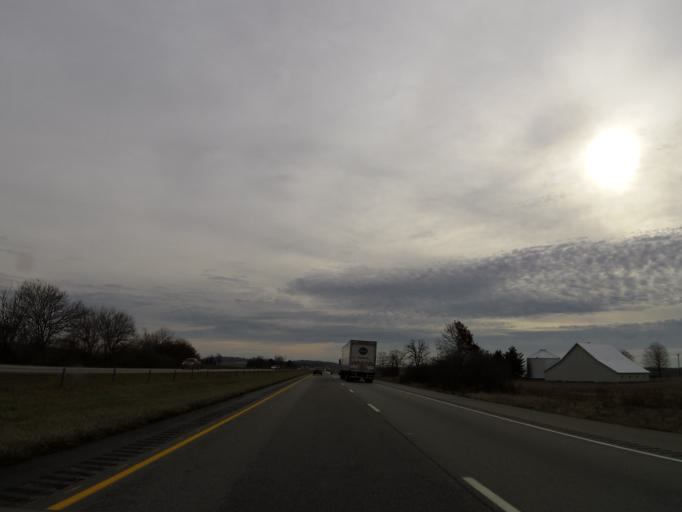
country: US
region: Indiana
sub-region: Montgomery County
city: Crawfordsville
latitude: 40.0633
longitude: -86.8418
